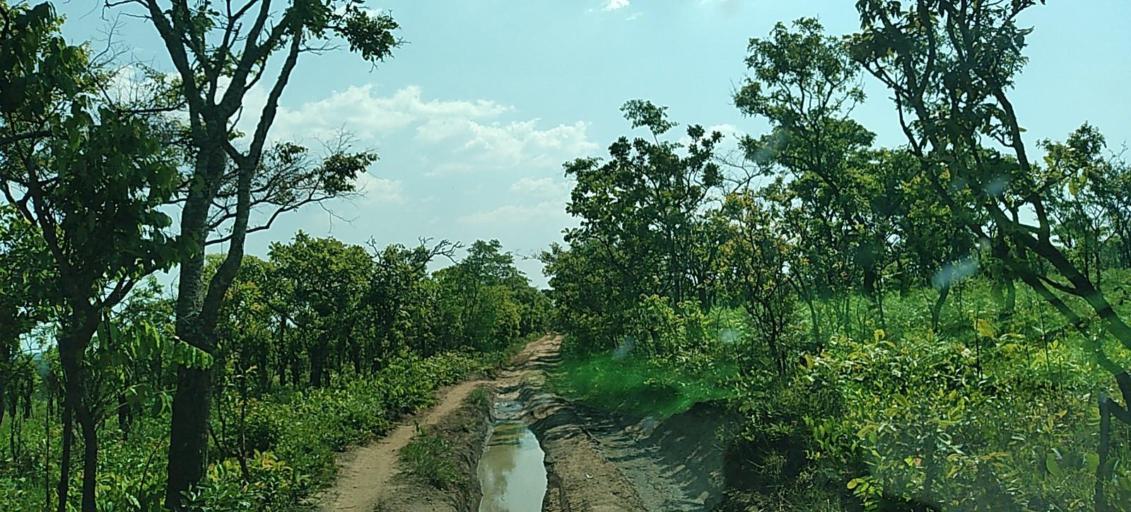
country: CD
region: Katanga
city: Kolwezi
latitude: -11.2680
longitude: 24.9965
